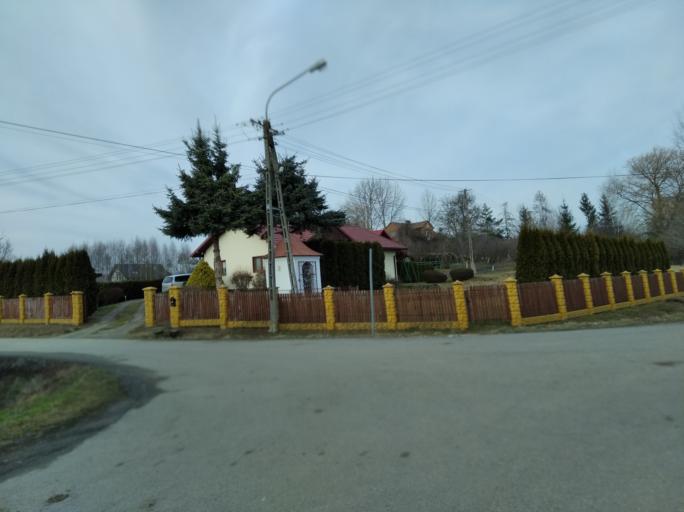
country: PL
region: Subcarpathian Voivodeship
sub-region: Powiat brzozowski
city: Gorki
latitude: 49.6520
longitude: 22.0322
